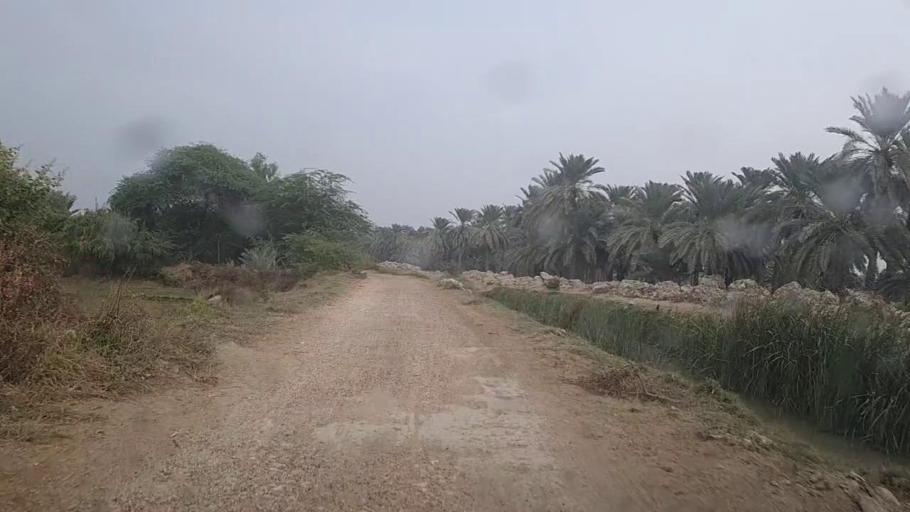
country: PK
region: Sindh
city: Gambat
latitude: 27.3888
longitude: 68.5936
